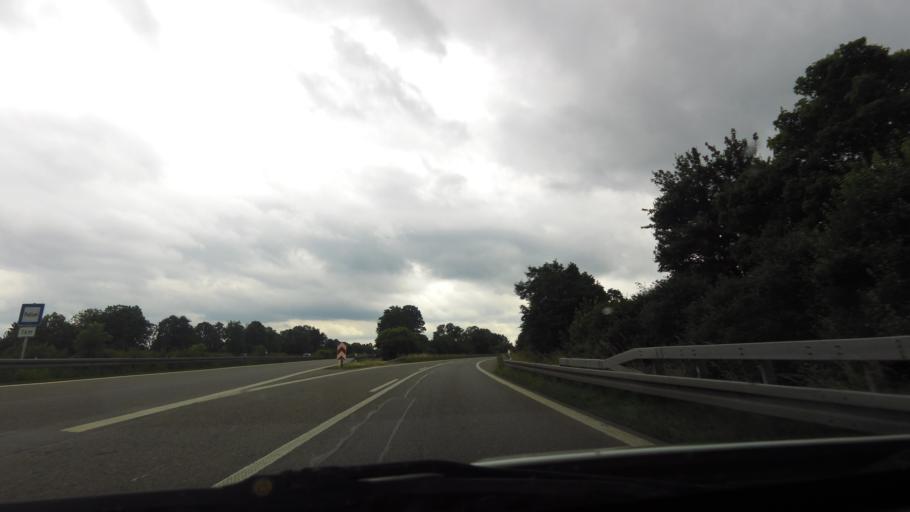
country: DE
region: Bavaria
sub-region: Swabia
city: Buxheim
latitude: 48.0000
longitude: 10.1495
